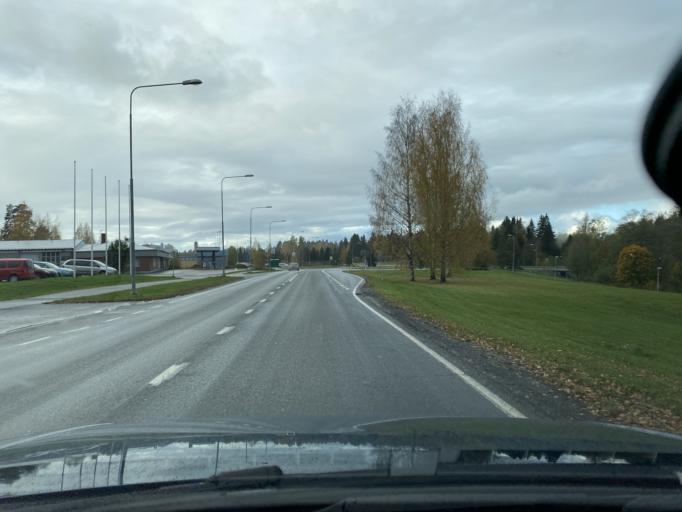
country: FI
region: Haeme
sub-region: Forssa
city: Forssa
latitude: 60.8238
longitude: 23.6012
